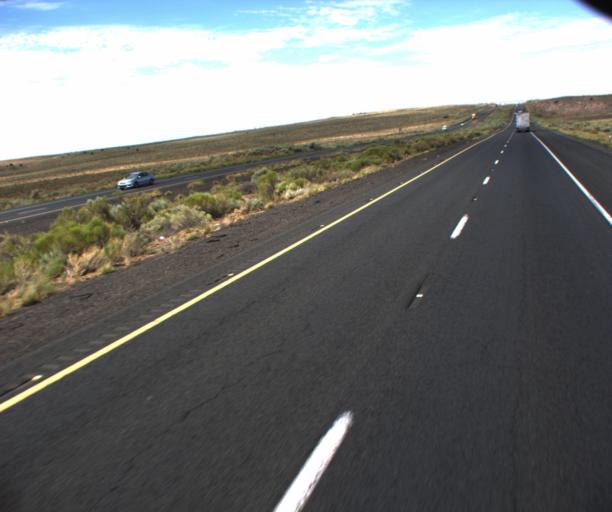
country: US
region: Arizona
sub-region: Apache County
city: Houck
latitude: 35.1019
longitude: -109.6254
